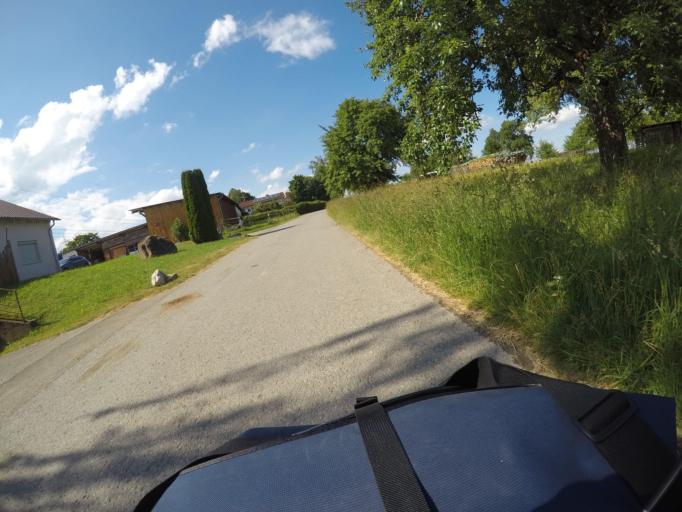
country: DE
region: Baden-Wuerttemberg
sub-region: Regierungsbezirk Stuttgart
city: Nufringen
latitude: 48.6359
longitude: 8.8735
